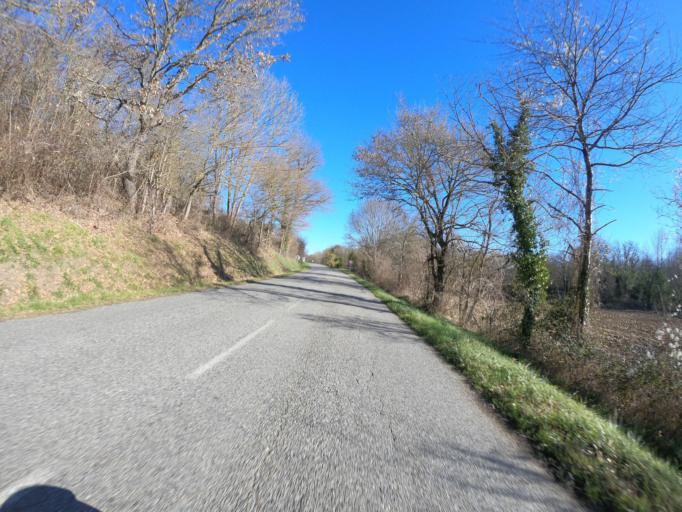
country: FR
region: Midi-Pyrenees
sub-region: Departement de l'Ariege
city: Mirepoix
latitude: 43.0835
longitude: 1.8209
